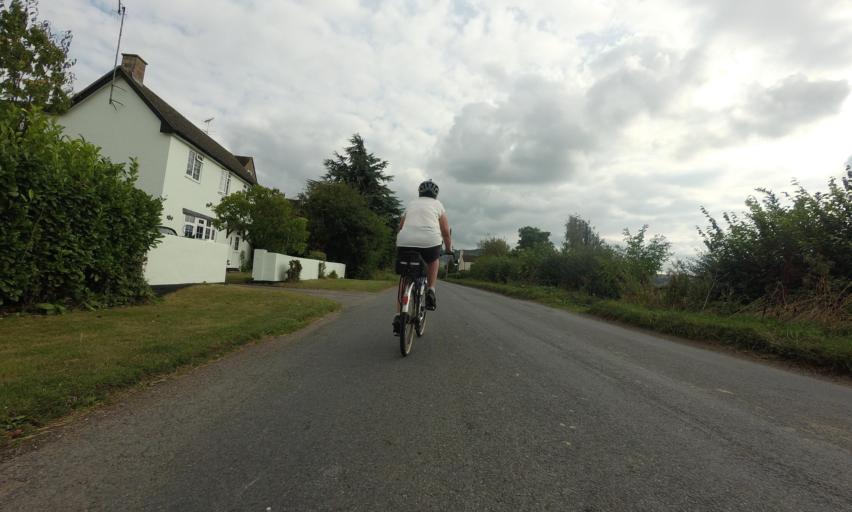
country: GB
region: England
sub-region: Gloucestershire
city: Winchcombe
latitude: 51.9840
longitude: -1.9983
